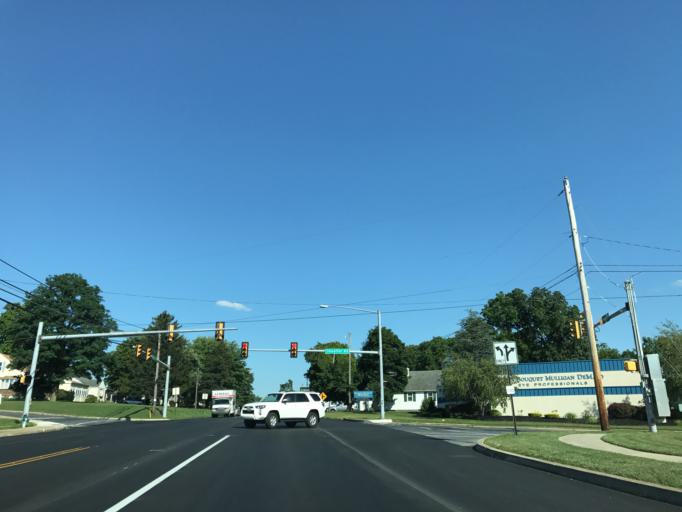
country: US
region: Pennsylvania
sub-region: Lancaster County
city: Rheems
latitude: 40.1377
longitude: -76.5838
